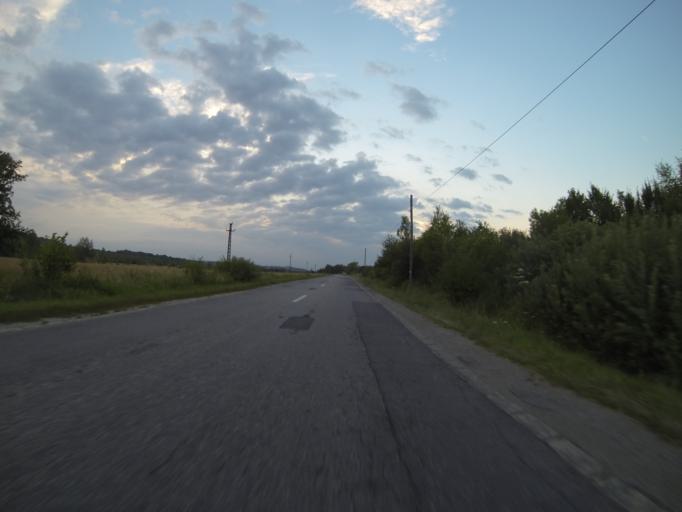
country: RO
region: Brasov
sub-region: Comuna Sinca Veche
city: Persani
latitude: 45.7411
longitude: 25.2157
